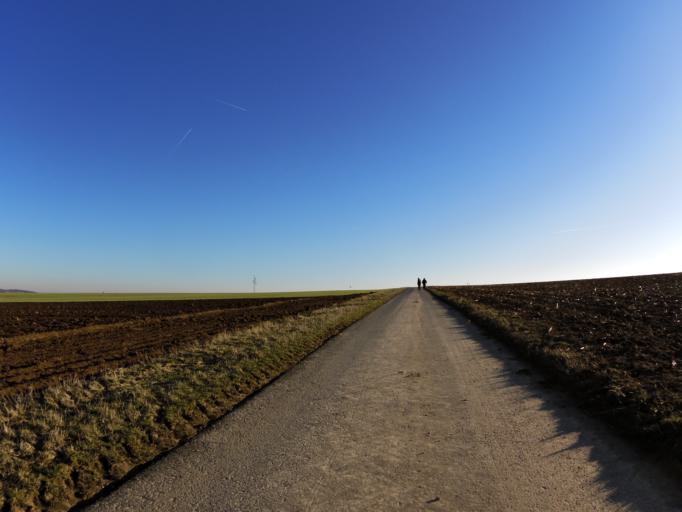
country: DE
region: Bavaria
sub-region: Regierungsbezirk Unterfranken
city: Estenfeld
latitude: 49.8449
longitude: 9.9989
